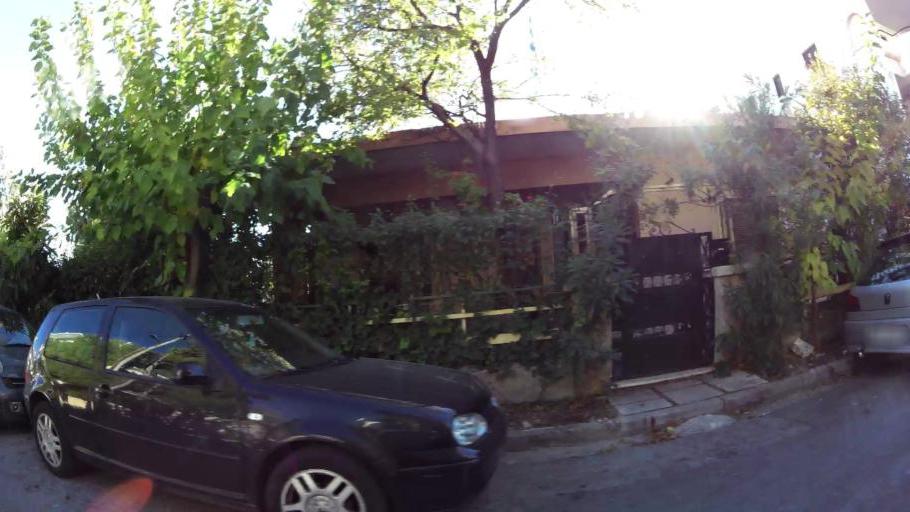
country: GR
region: Attica
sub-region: Nomarchia Athinas
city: Melissia
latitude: 38.0463
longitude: 23.8439
